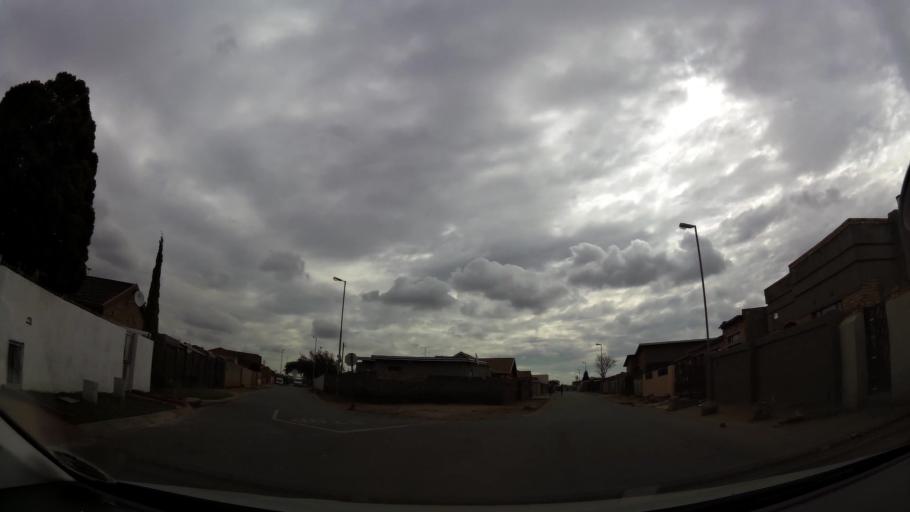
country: ZA
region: Gauteng
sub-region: City of Johannesburg Metropolitan Municipality
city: Soweto
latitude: -26.2778
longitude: 27.8610
